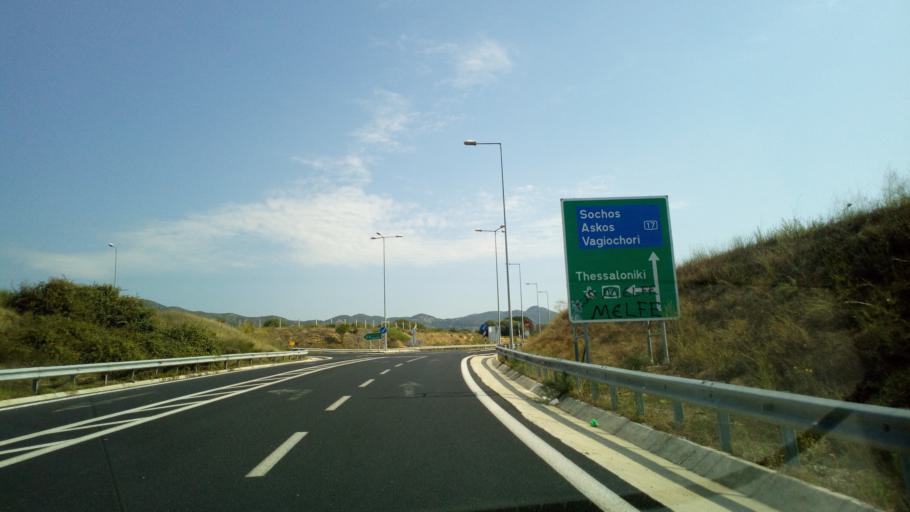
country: GR
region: Central Macedonia
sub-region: Nomos Thessalonikis
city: Askos
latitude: 40.7013
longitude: 23.3699
